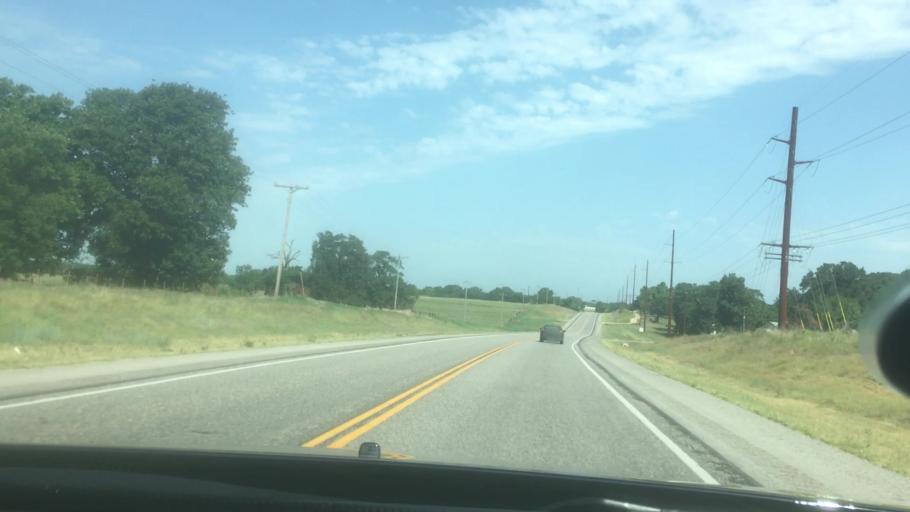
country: US
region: Oklahoma
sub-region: Seminole County
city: Konawa
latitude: 34.8554
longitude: -96.8176
